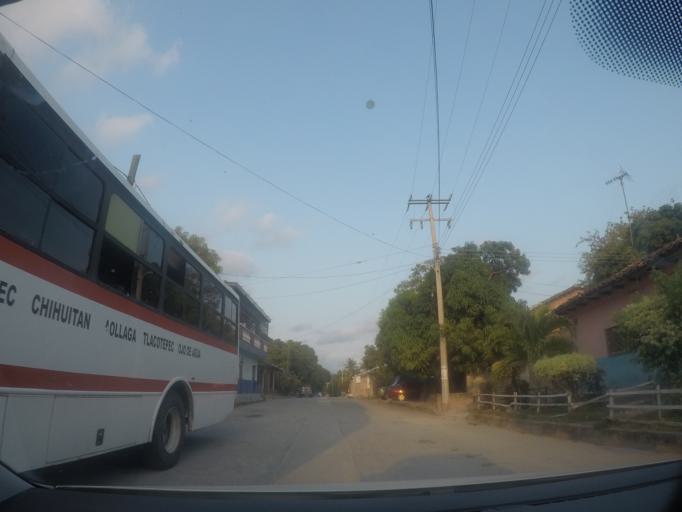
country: MX
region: Oaxaca
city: San Pedro Comitancillo
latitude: 16.5834
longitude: -95.2073
